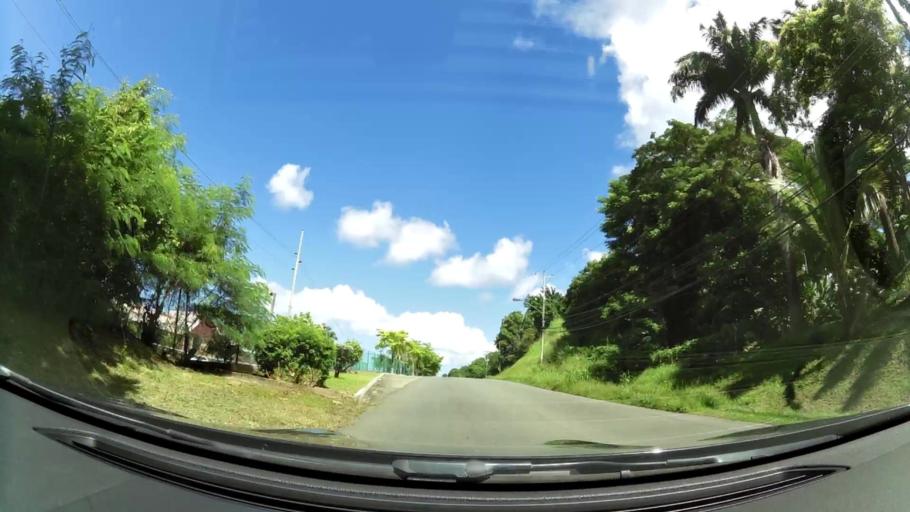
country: TT
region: Tobago
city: Scarborough
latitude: 11.2010
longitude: -60.7862
